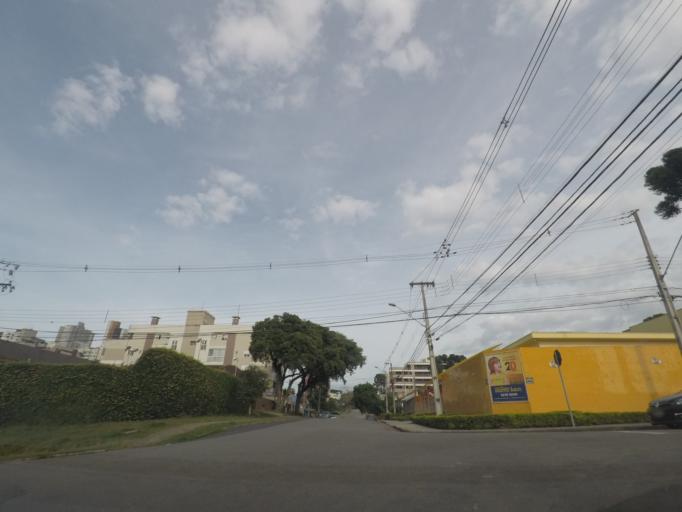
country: BR
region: Parana
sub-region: Curitiba
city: Curitiba
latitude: -25.4296
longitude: -49.2989
